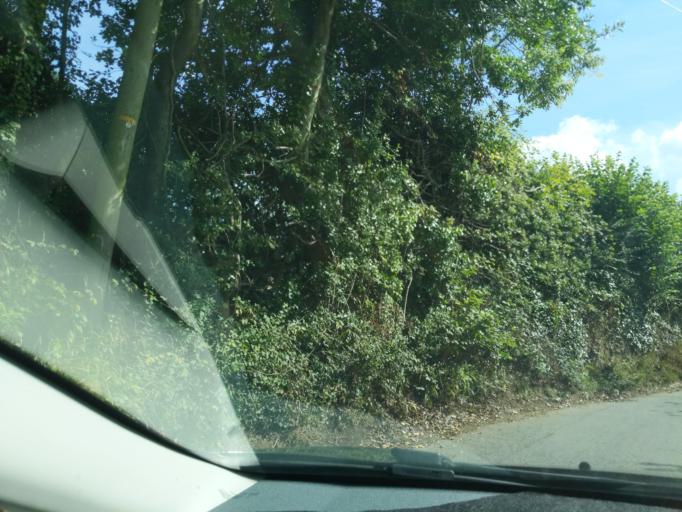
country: GB
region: England
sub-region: Cornwall
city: Torpoint
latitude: 50.3596
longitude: -4.2360
